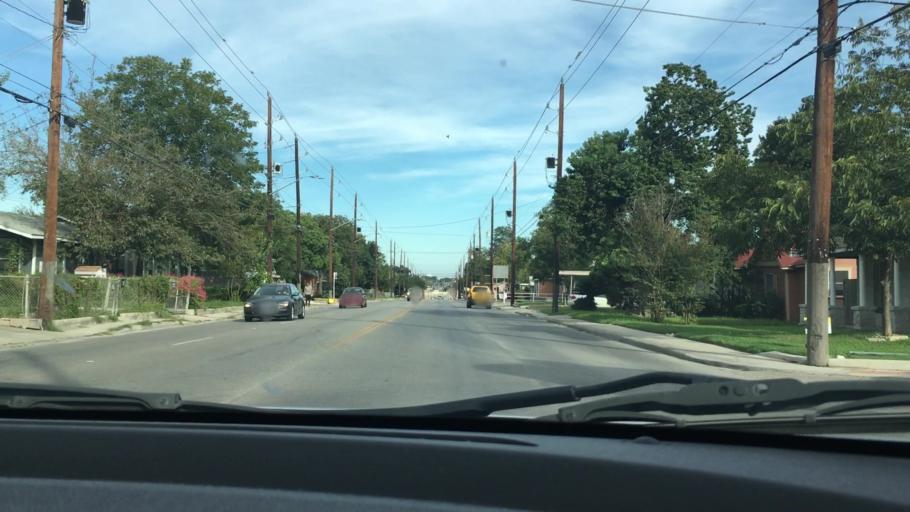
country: US
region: Texas
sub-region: Bexar County
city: Balcones Heights
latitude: 29.4664
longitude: -98.5233
